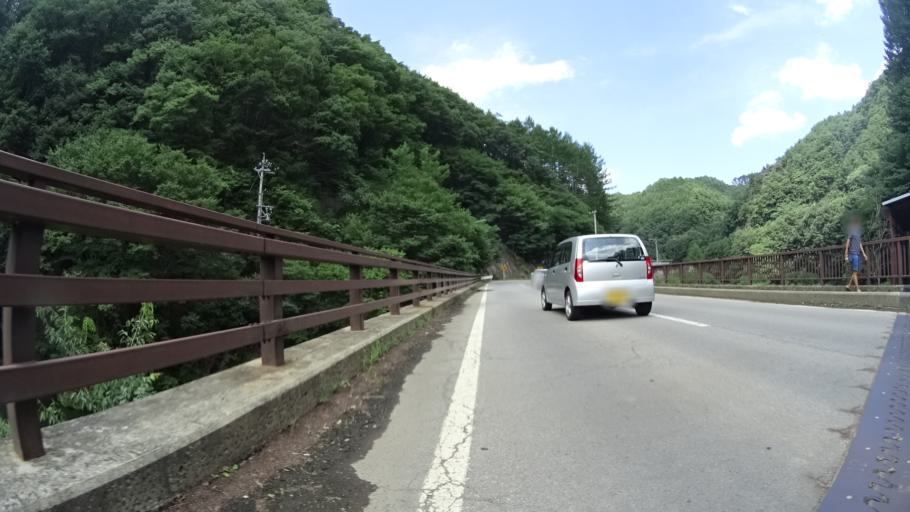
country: JP
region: Nagano
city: Saku
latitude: 36.0631
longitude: 138.5029
